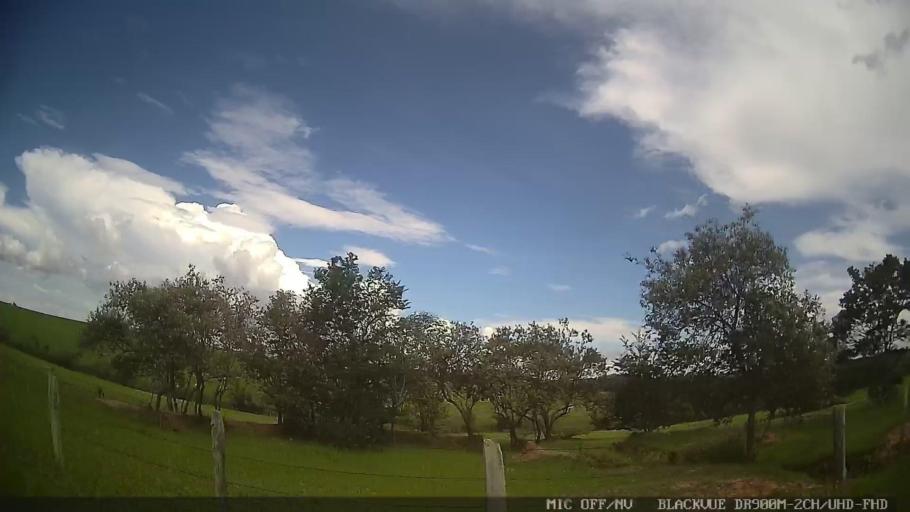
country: BR
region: Sao Paulo
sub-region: Conchas
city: Conchas
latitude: -22.9770
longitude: -47.9882
